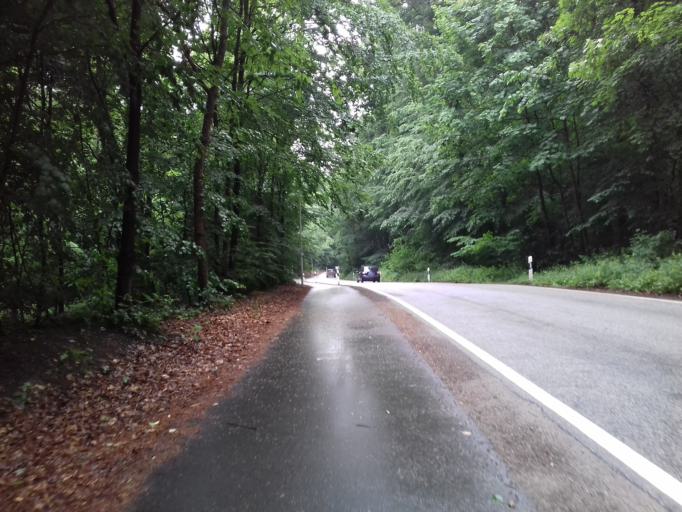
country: DE
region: Schleswig-Holstein
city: Kronshagen
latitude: 54.3228
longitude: 10.0735
